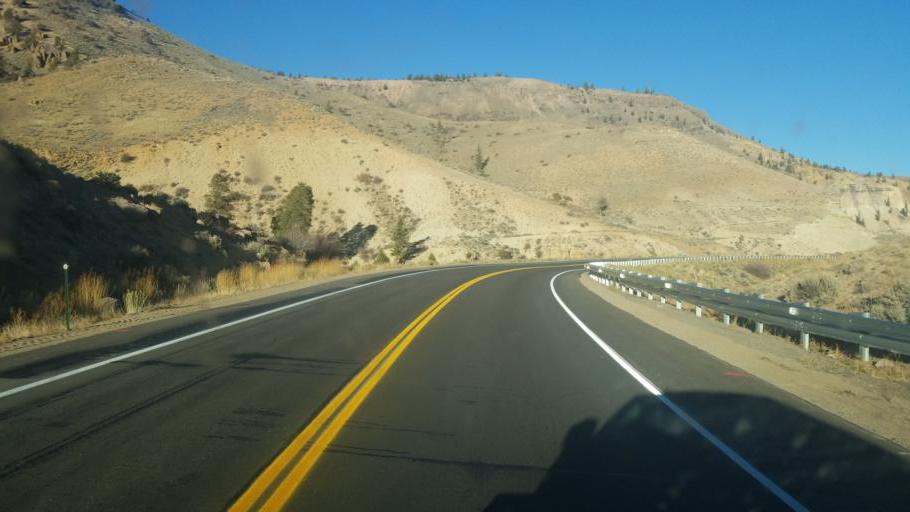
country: US
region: Colorado
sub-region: Gunnison County
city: Gunnison
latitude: 38.4812
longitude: -107.2124
